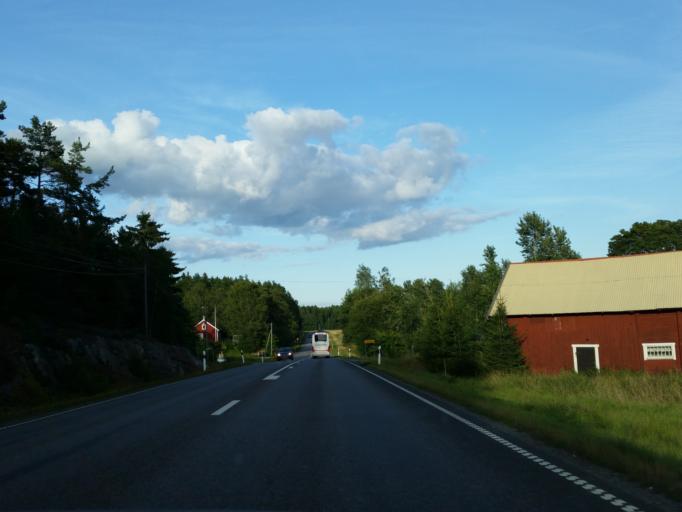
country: SE
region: Stockholm
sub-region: Sodertalje Kommun
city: Molnbo
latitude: 59.0614
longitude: 17.5010
